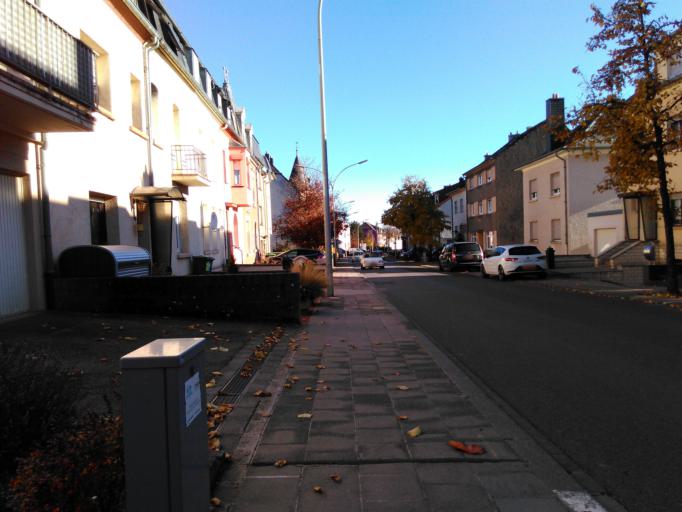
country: LU
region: Luxembourg
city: Belvaux
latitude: 49.5074
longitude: 5.9272
